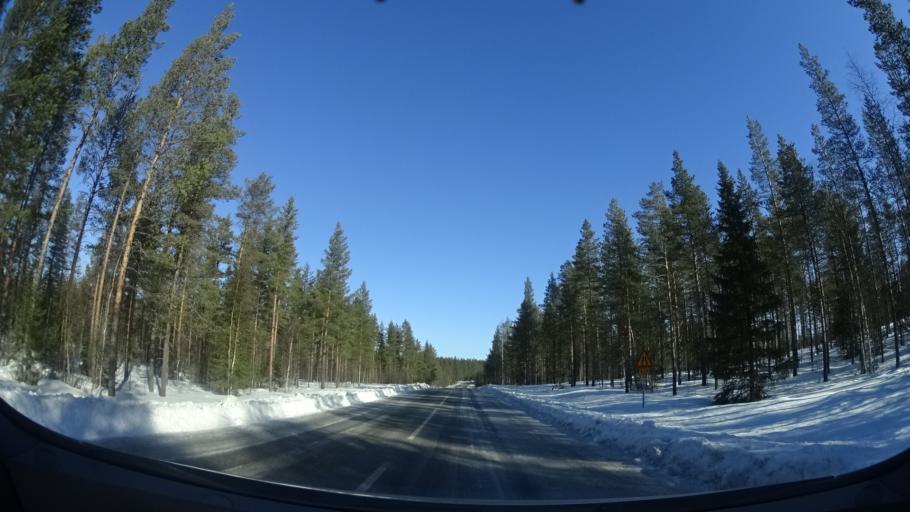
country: SE
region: Vaesterbotten
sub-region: Skelleftea Kommun
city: Langsele
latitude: 65.0739
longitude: 20.0605
